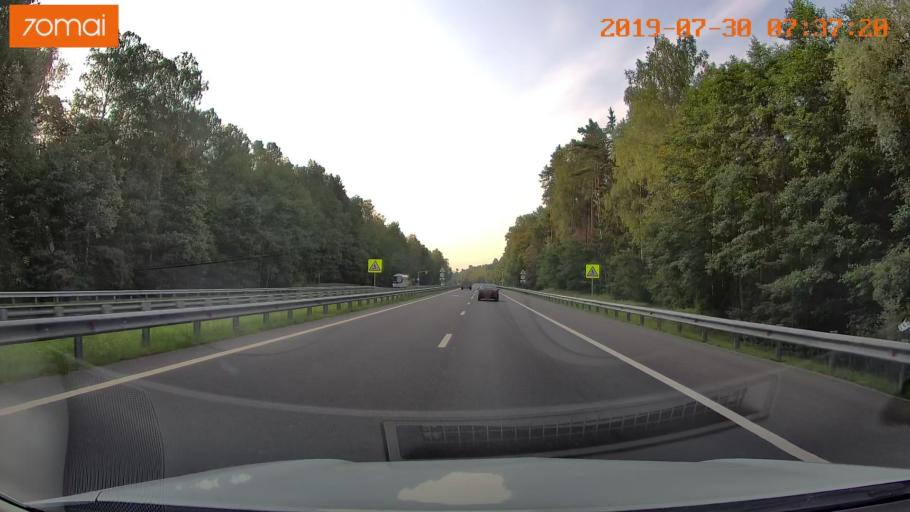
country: RU
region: Kaliningrad
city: Gvardeysk
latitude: 54.6565
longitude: 21.1444
